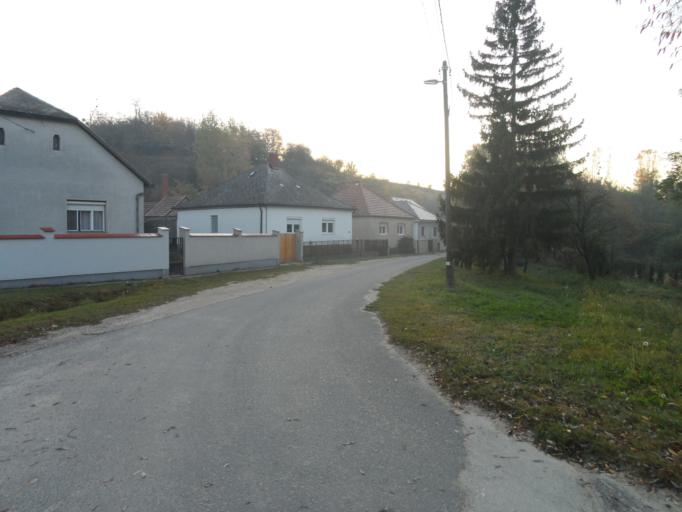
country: HU
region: Veszprem
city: Ajka
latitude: 47.1699
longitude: 17.5520
